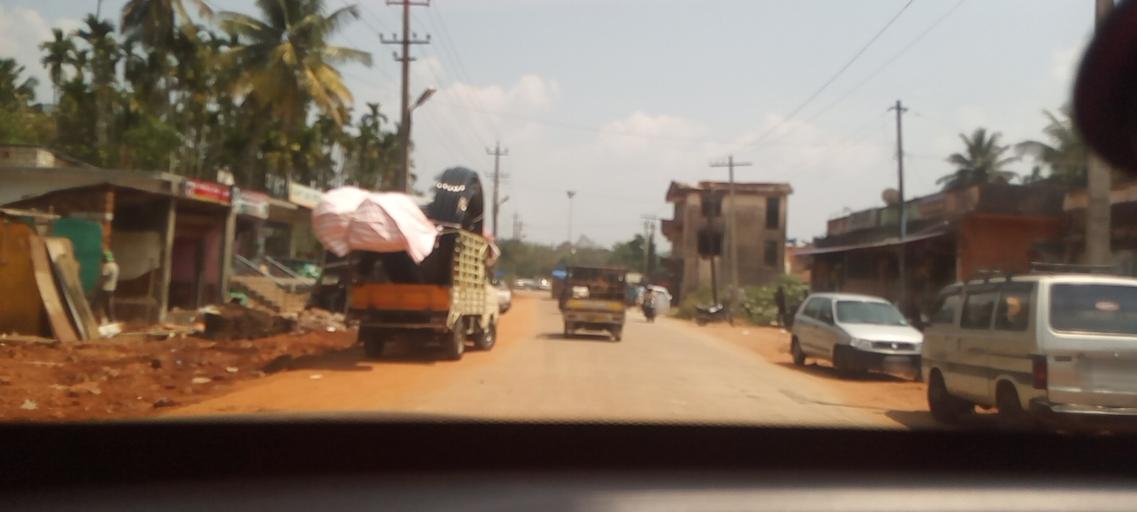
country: IN
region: Karnataka
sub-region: Chikmagalur
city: Koppa
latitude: 13.3498
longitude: 75.4685
